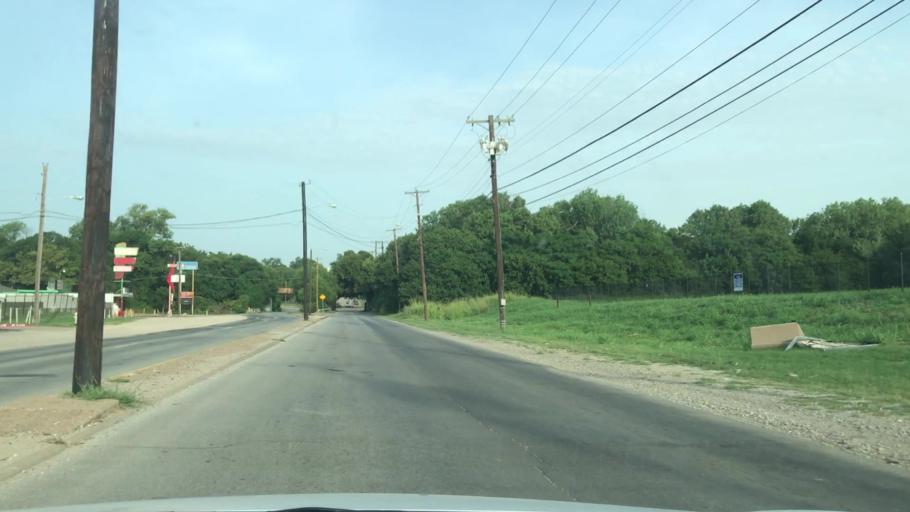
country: US
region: Texas
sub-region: Dallas County
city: Dallas
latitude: 32.7837
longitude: -96.7308
